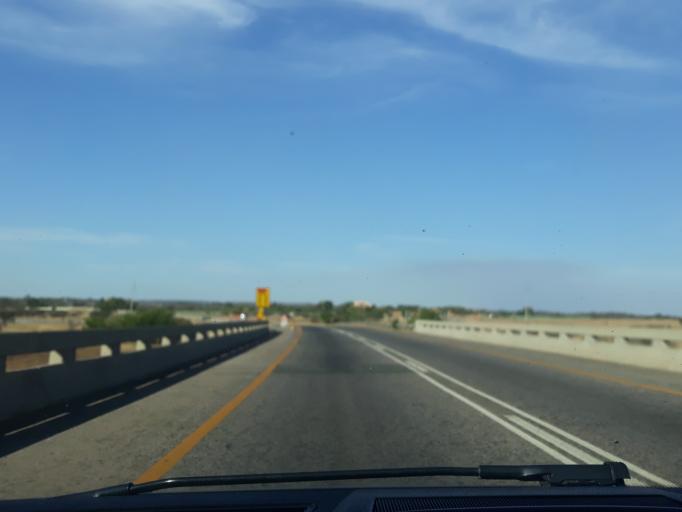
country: ZA
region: Limpopo
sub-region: Capricorn District Municipality
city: Polokwane
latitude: -23.9456
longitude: 29.4154
